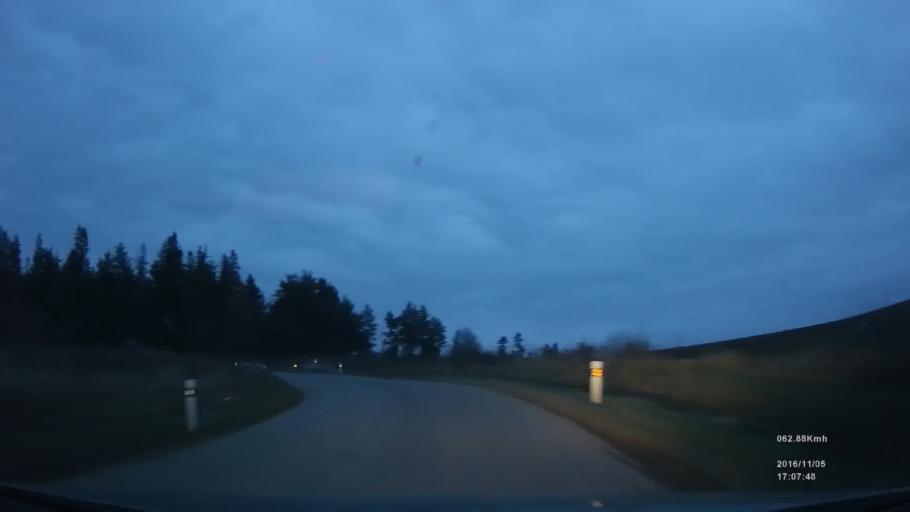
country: SK
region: Presovsky
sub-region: Okres Presov
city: Levoca
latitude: 49.0464
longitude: 20.5081
